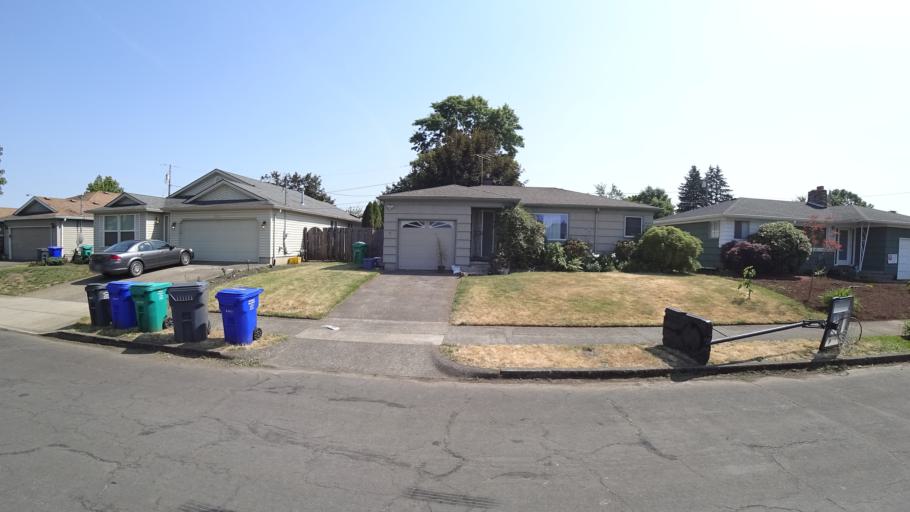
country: US
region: Oregon
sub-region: Multnomah County
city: Lents
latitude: 45.5138
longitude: -122.5669
